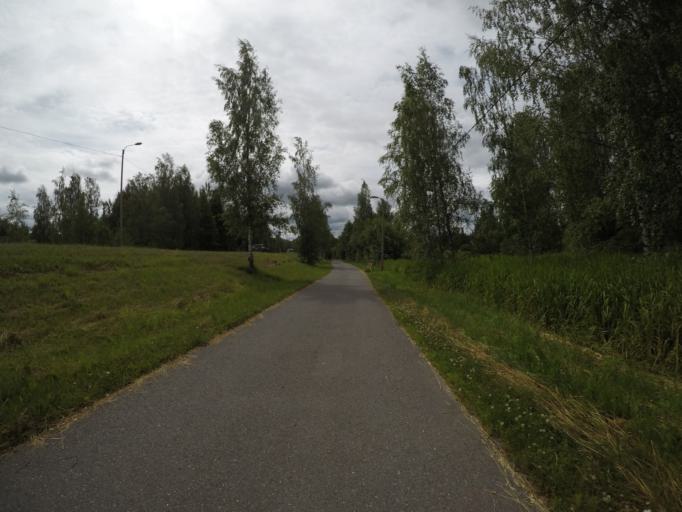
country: FI
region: Haeme
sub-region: Haemeenlinna
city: Haemeenlinna
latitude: 61.0015
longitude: 24.5016
